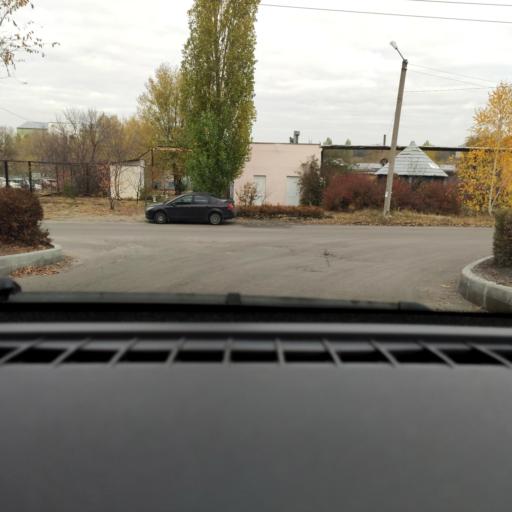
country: RU
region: Voronezj
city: Pridonskoy
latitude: 51.6391
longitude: 39.1070
